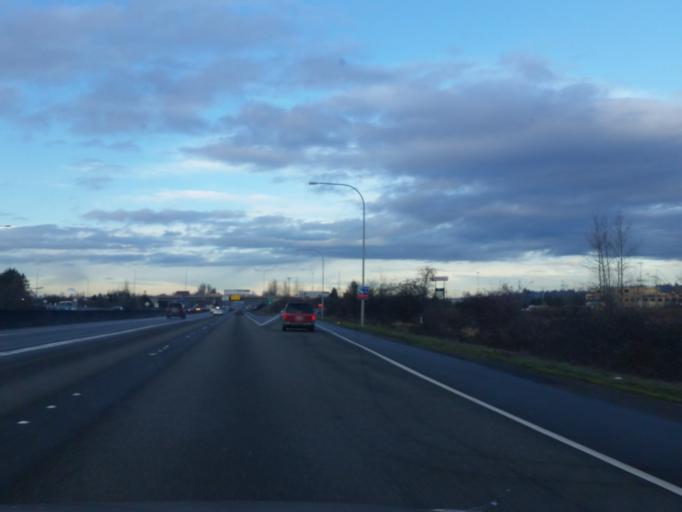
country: US
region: Washington
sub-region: King County
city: Kent
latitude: 47.3500
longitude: -122.2446
